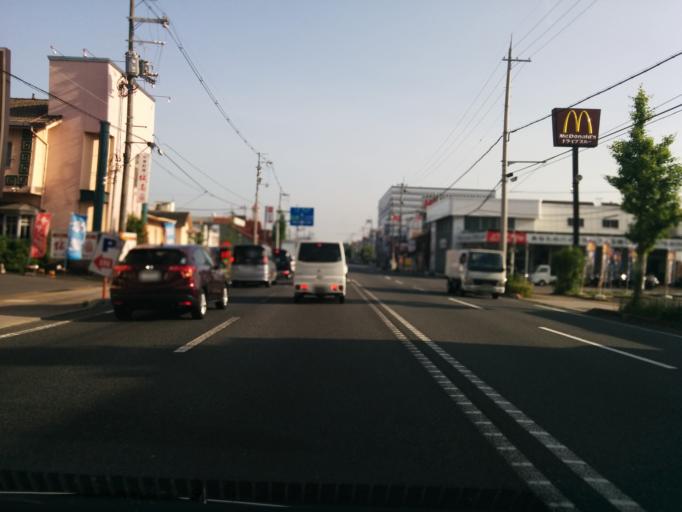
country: JP
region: Kyoto
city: Muko
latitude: 34.9478
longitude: 135.7454
